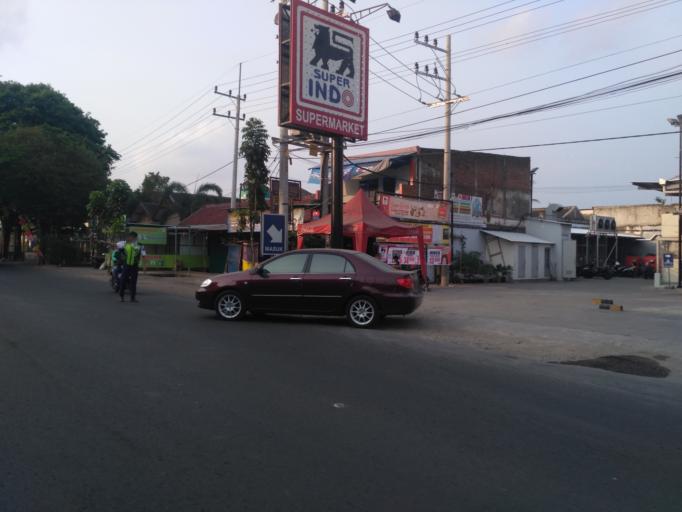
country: ID
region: East Java
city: Kebonsari
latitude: -8.0142
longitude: 112.6204
